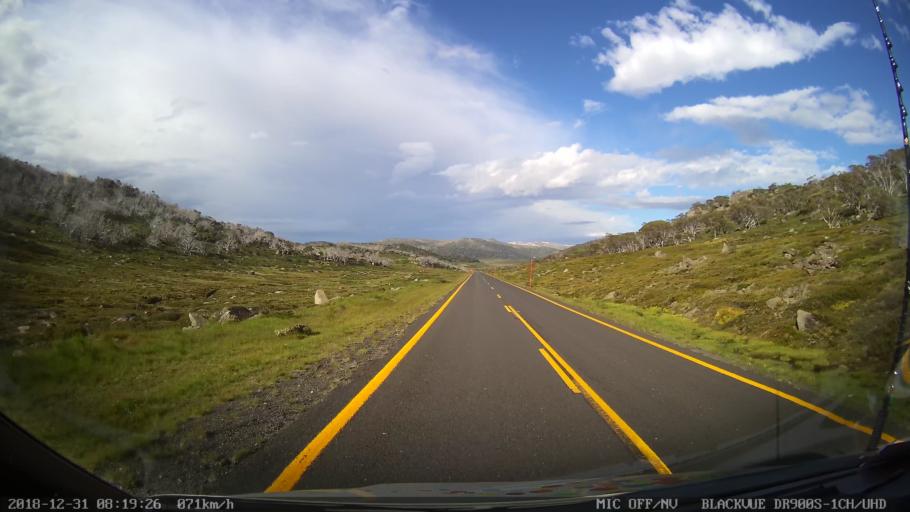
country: AU
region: New South Wales
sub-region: Snowy River
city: Jindabyne
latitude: -36.4192
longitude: 148.3858
